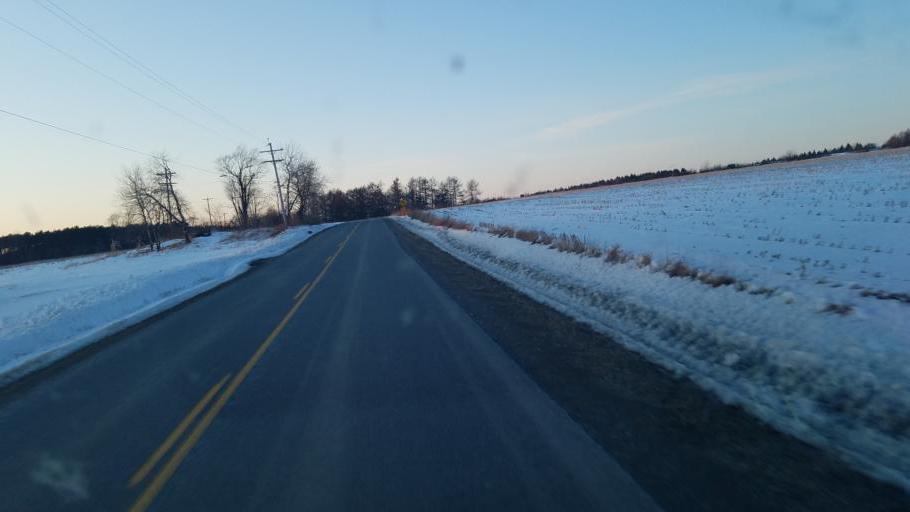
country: US
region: Pennsylvania
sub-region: Tioga County
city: Westfield
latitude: 42.0045
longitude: -77.6941
